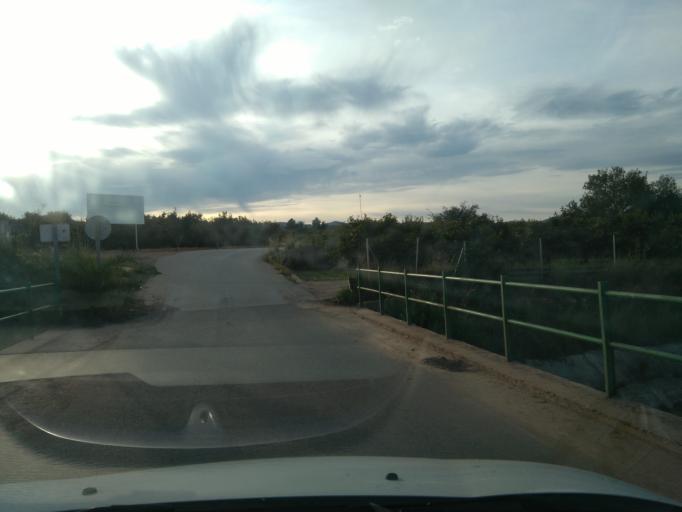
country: ES
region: Valencia
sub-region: Provincia de Valencia
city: Benimodo
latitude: 39.2002
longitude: -0.5667
